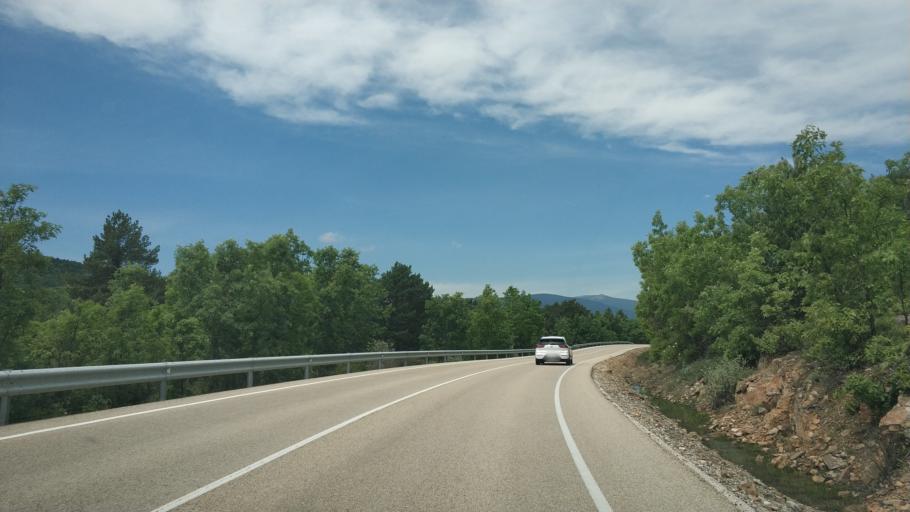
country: ES
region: Castille and Leon
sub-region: Provincia de Soria
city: Vinuesa
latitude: 41.8860
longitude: -2.7256
